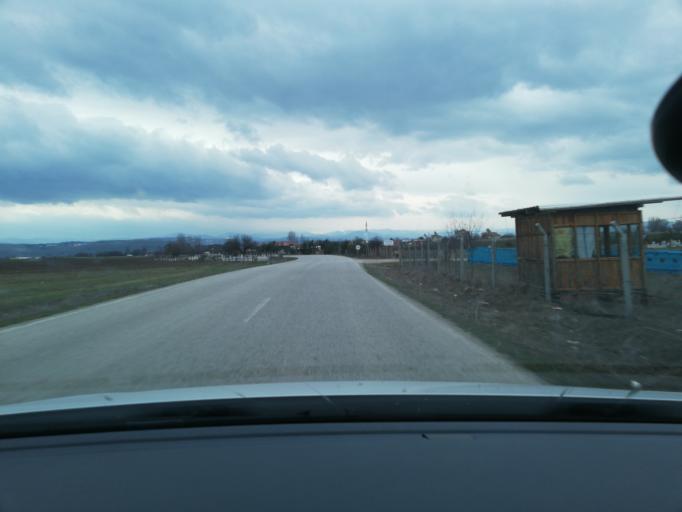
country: TR
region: Bolu
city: Gerede
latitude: 40.7641
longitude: 32.1989
